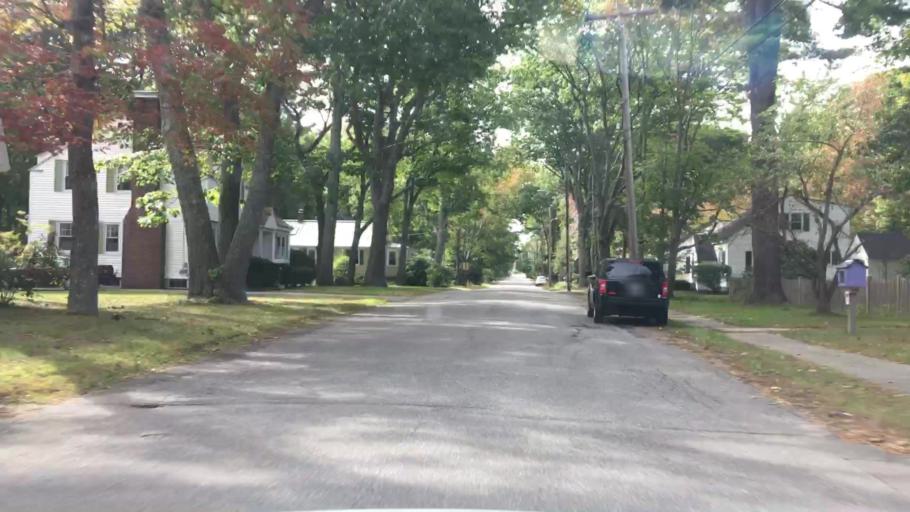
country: US
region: Maine
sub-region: Cumberland County
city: Brunswick
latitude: 43.9039
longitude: -69.9708
